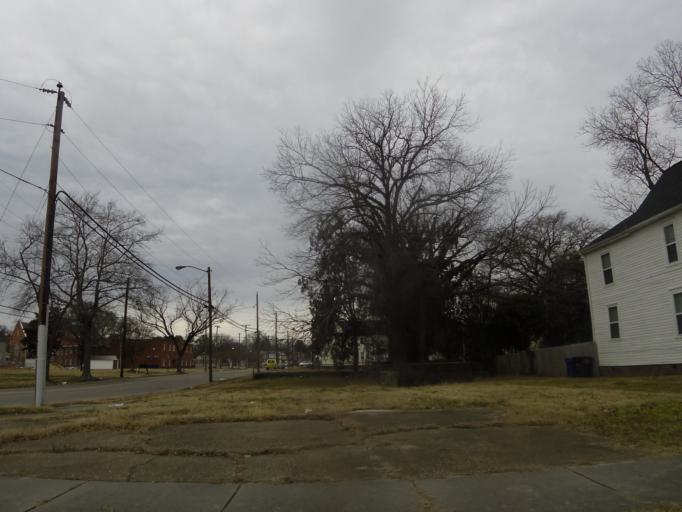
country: US
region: Virginia
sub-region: City of Portsmouth
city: Portsmouth
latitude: 36.8356
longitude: -76.3255
